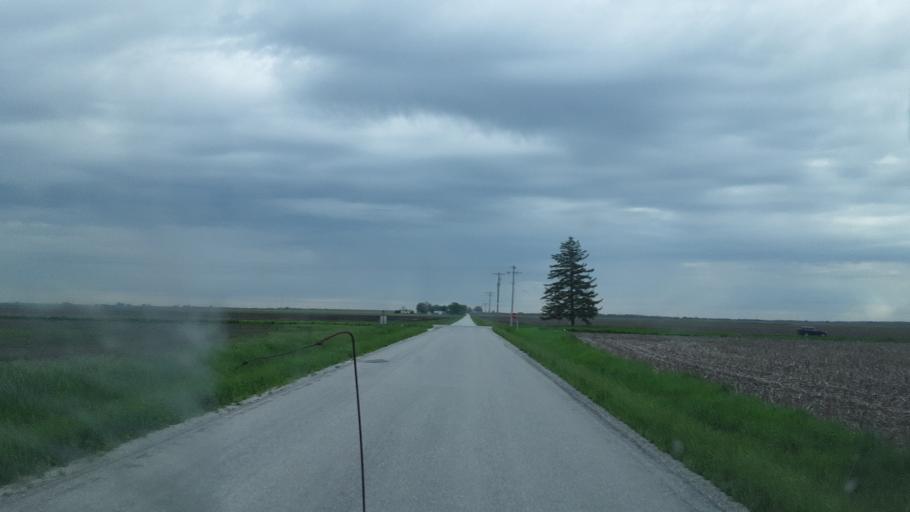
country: US
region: Illinois
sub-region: McDonough County
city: Bushnell
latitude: 40.3806
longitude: -90.5078
